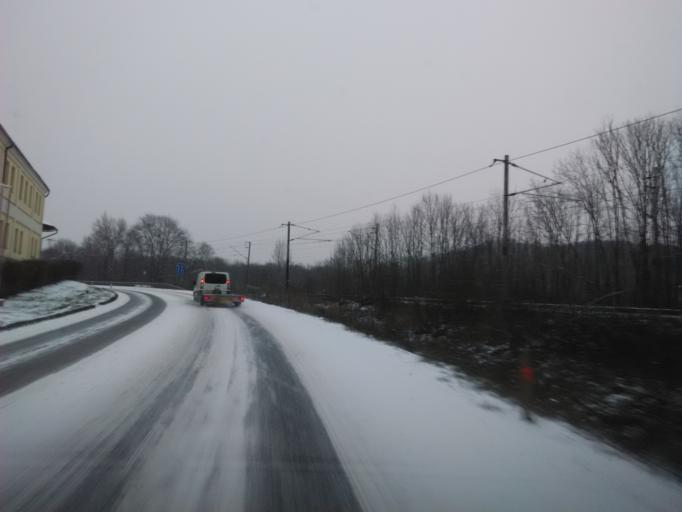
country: CZ
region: Olomoucky
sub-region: Okres Prerov
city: Hranice
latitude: 49.5272
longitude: 17.7513
